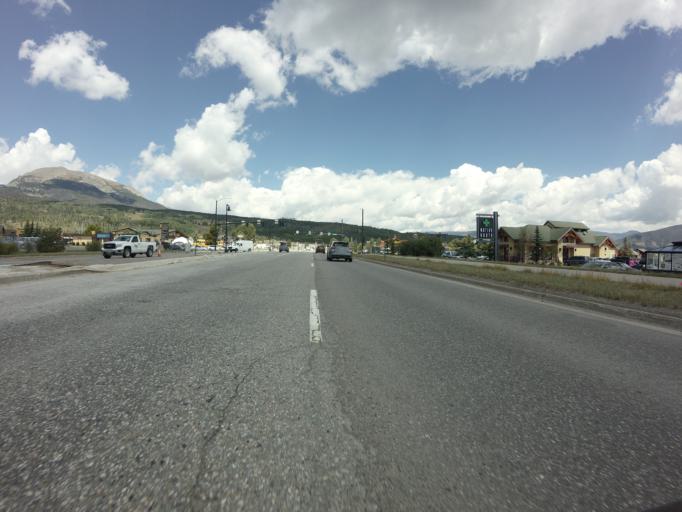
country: US
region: Colorado
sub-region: Summit County
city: Frisco
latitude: 39.5873
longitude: -106.0947
